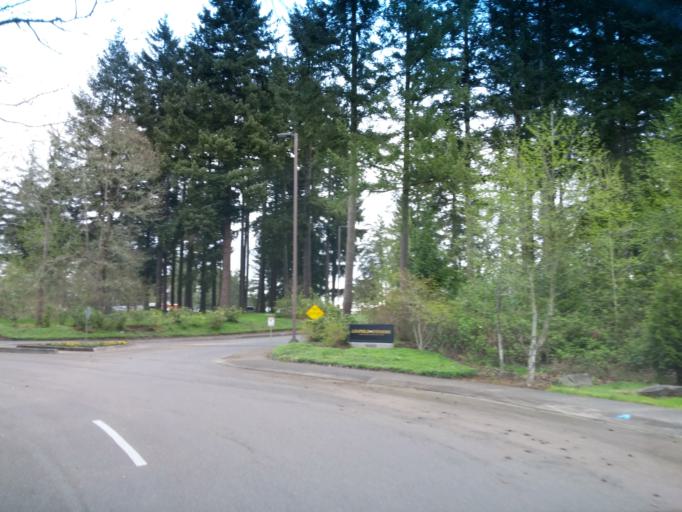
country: US
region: Oregon
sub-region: Washington County
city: Cedar Mill
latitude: 45.5245
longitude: -122.8260
